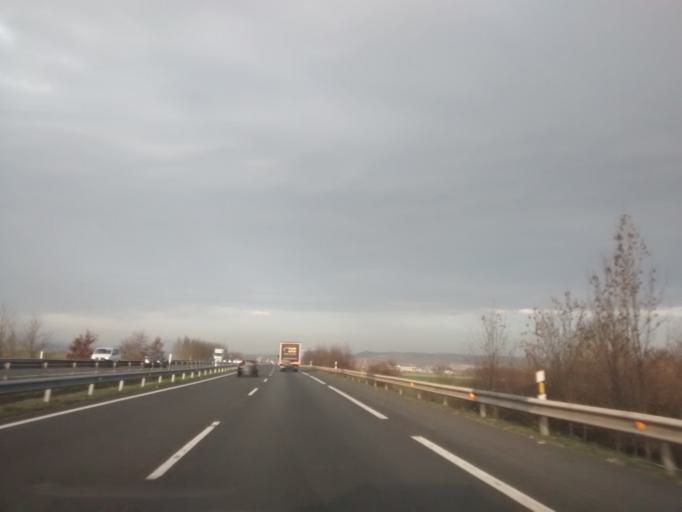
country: ES
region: Basque Country
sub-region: Provincia de Alava
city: Gasteiz / Vitoria
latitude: 42.8715
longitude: -2.7200
